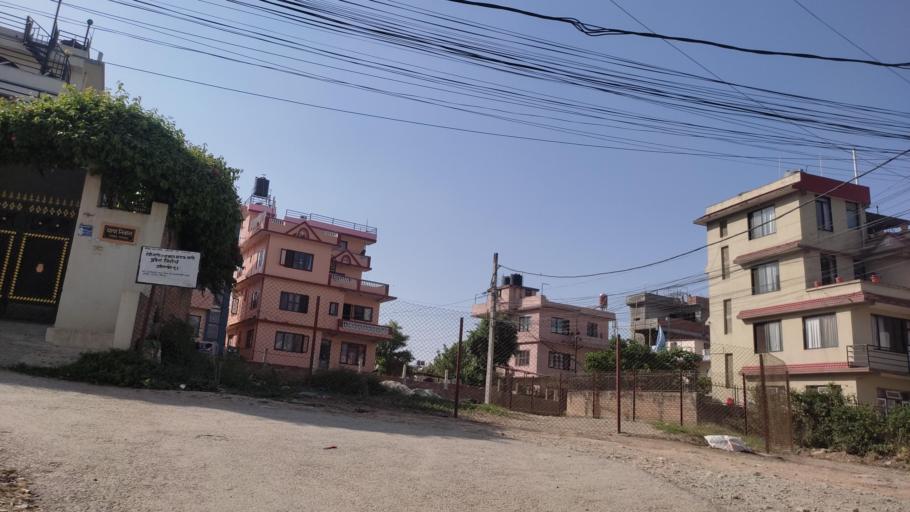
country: NP
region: Central Region
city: Kirtipur
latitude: 27.6657
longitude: 85.2674
